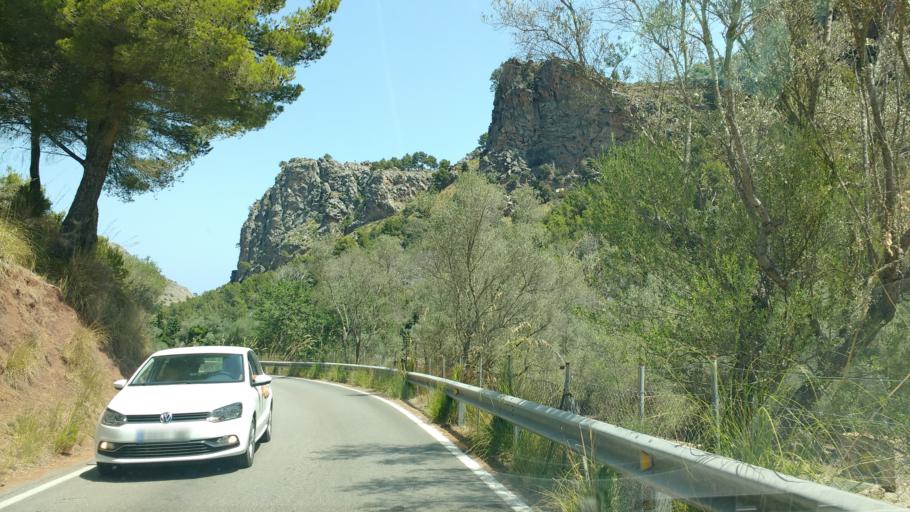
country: ES
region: Balearic Islands
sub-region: Illes Balears
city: Escorca
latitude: 39.8454
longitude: 2.7966
